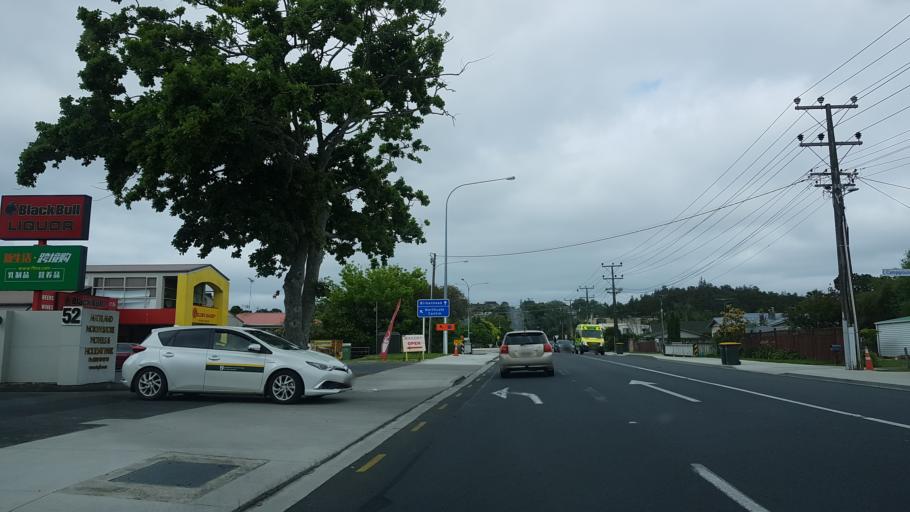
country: NZ
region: Auckland
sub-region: Auckland
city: North Shore
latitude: -36.7933
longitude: 174.7463
